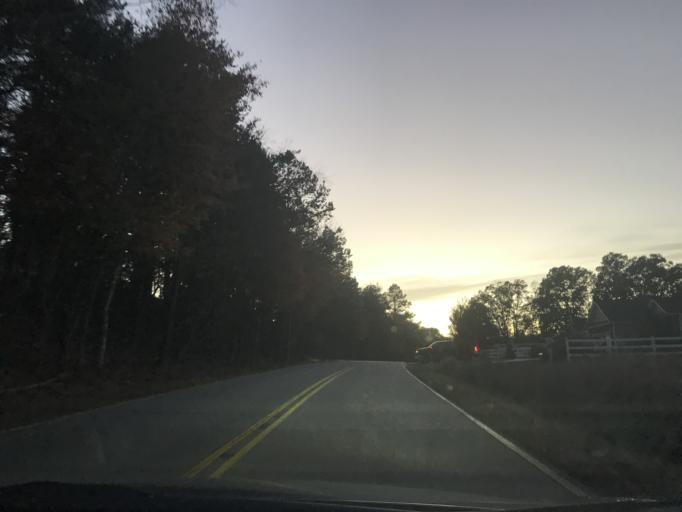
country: US
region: South Carolina
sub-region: Spartanburg County
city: Mayo
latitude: 35.0884
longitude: -81.8895
